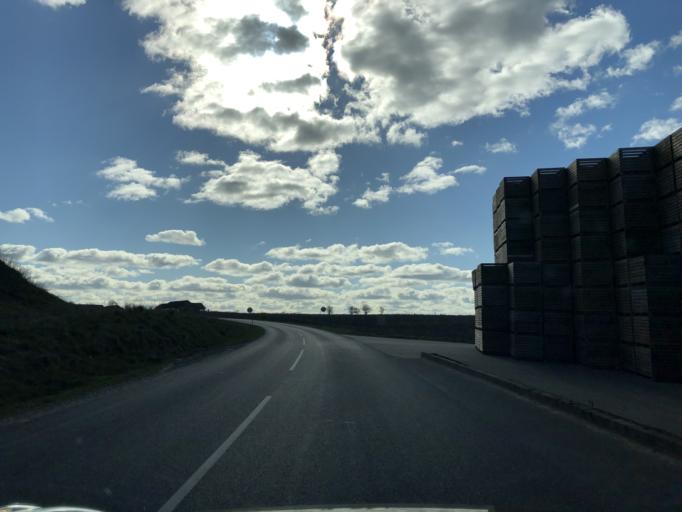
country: DK
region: North Denmark
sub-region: Vesthimmerland Kommune
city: Alestrup
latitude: 56.6081
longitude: 9.5413
